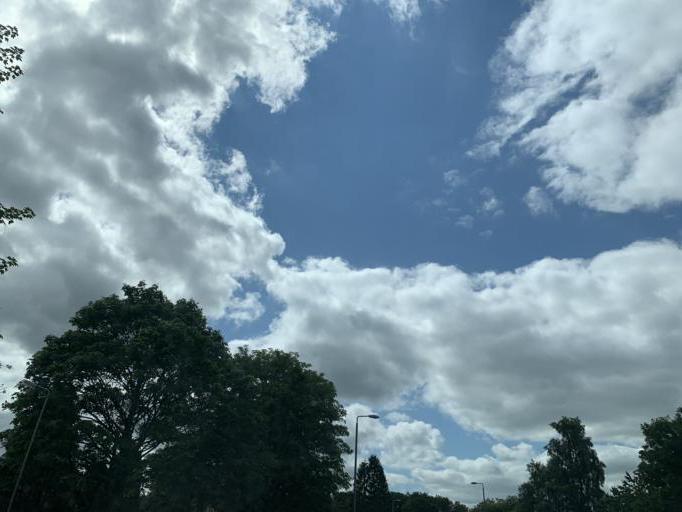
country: GB
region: Scotland
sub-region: East Renfrewshire
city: Newton Mearns
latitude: 55.7788
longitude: -4.3358
